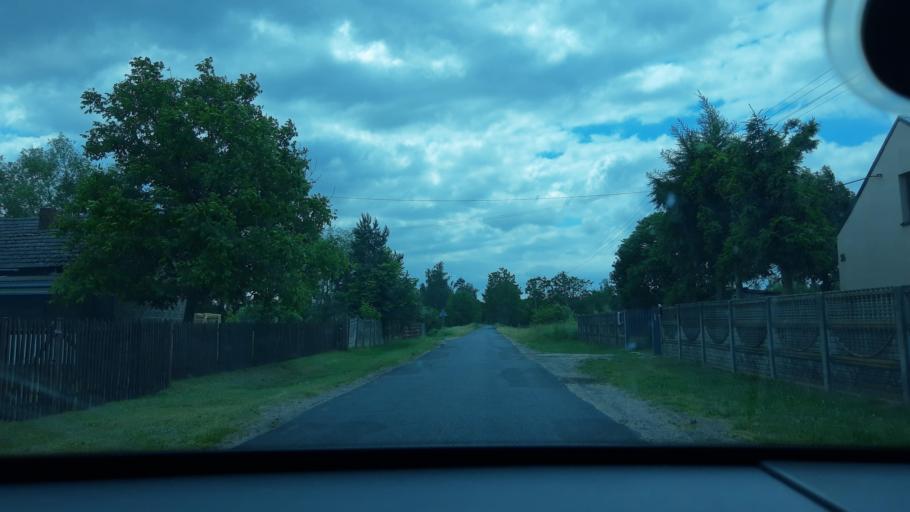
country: PL
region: Lodz Voivodeship
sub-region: Powiat sieradzki
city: Burzenin
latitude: 51.5047
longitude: 18.8472
